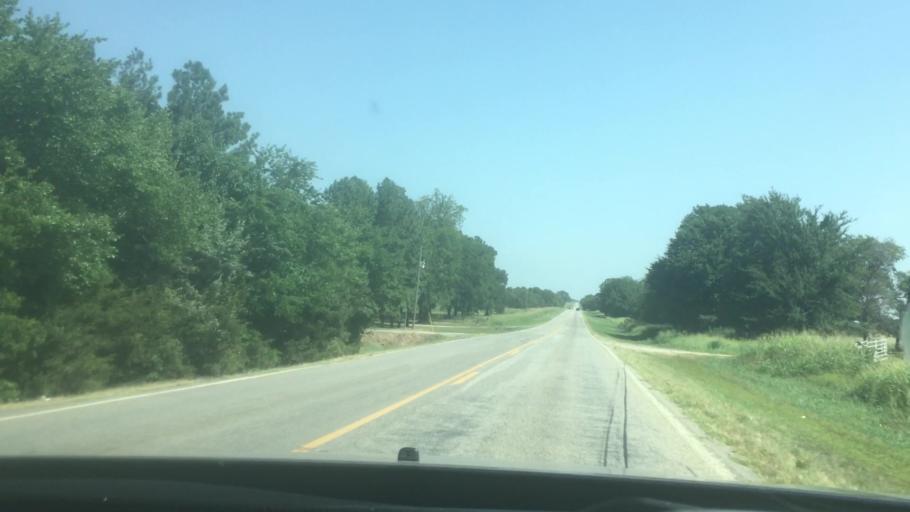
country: US
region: Oklahoma
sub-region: Johnston County
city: Tishomingo
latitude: 34.2874
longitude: -96.4248
